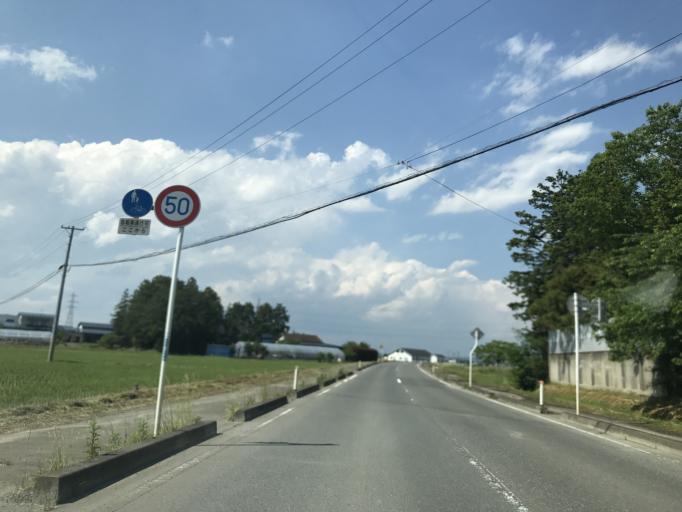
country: JP
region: Miyagi
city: Matsushima
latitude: 38.4491
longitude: 141.1114
